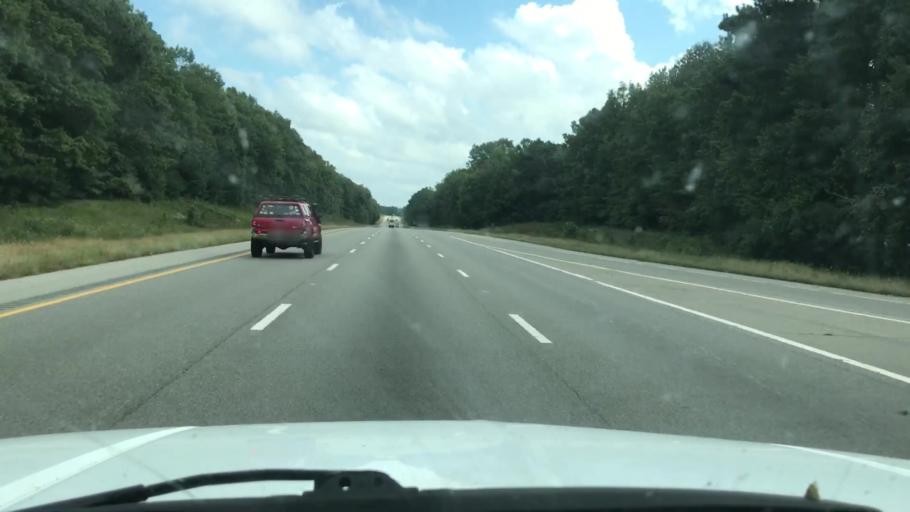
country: US
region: Virginia
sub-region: Henrico County
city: Short Pump
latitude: 37.6724
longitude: -77.5744
